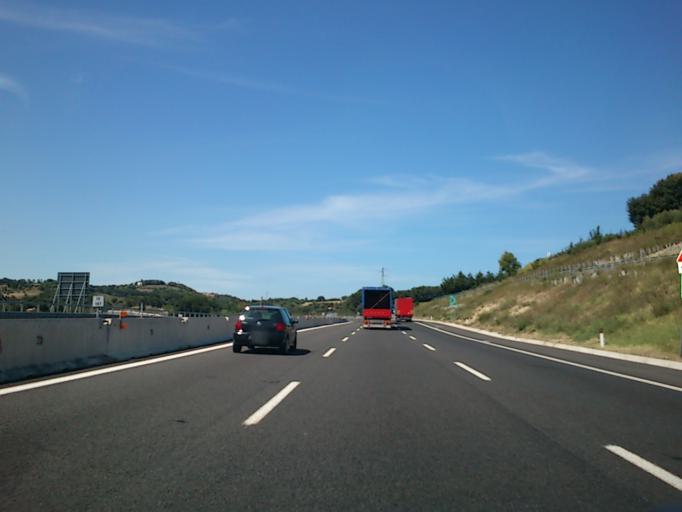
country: IT
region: The Marches
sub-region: Provincia di Pesaro e Urbino
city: Fenile
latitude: 43.8492
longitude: 12.9624
